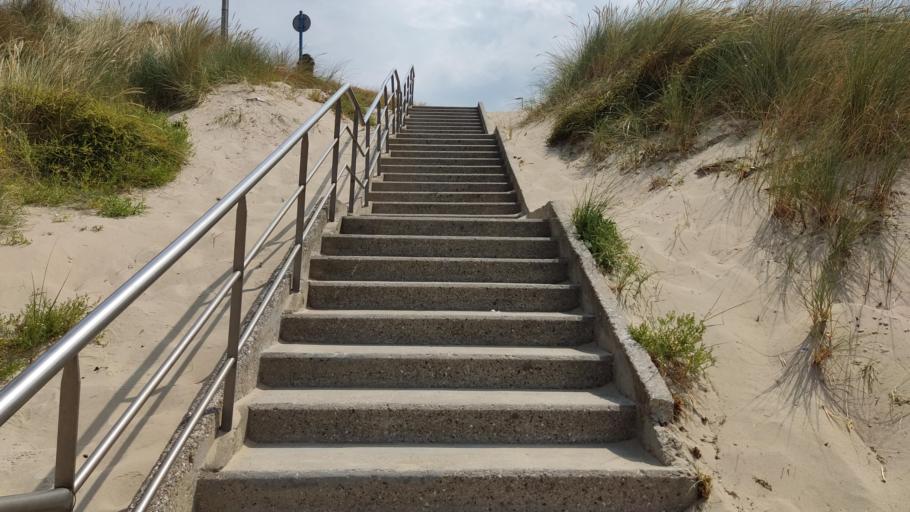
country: FR
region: Nord-Pas-de-Calais
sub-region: Departement du Pas-de-Calais
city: Le Portel
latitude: 50.7099
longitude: 1.5703
